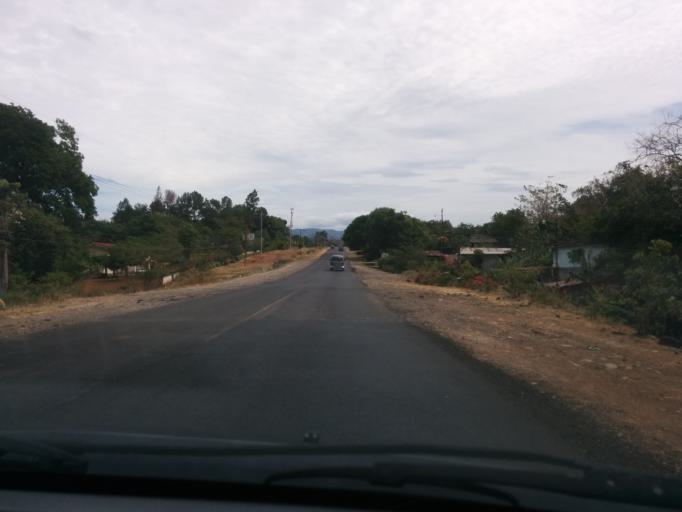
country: CR
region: Puntarenas
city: Esparza
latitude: 9.9981
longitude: -84.6545
